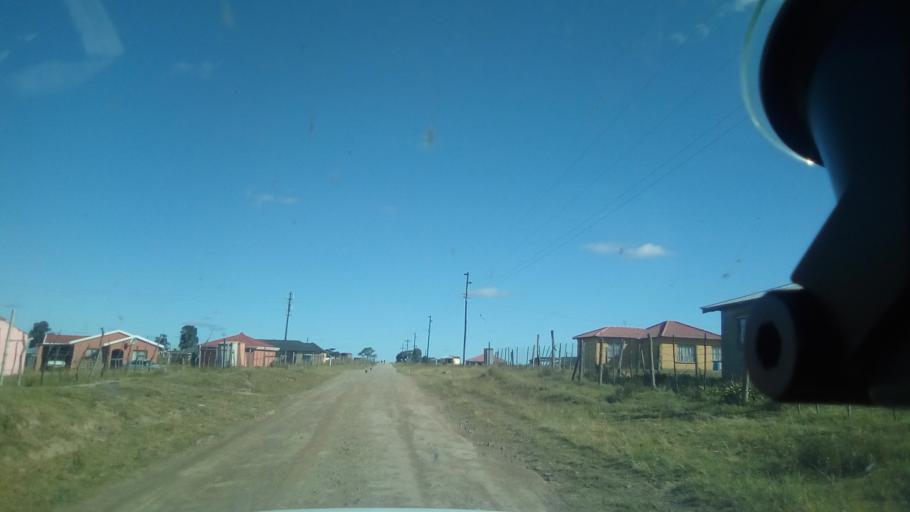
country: ZA
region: Eastern Cape
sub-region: Buffalo City Metropolitan Municipality
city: Bhisho
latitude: -32.7871
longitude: 27.3270
